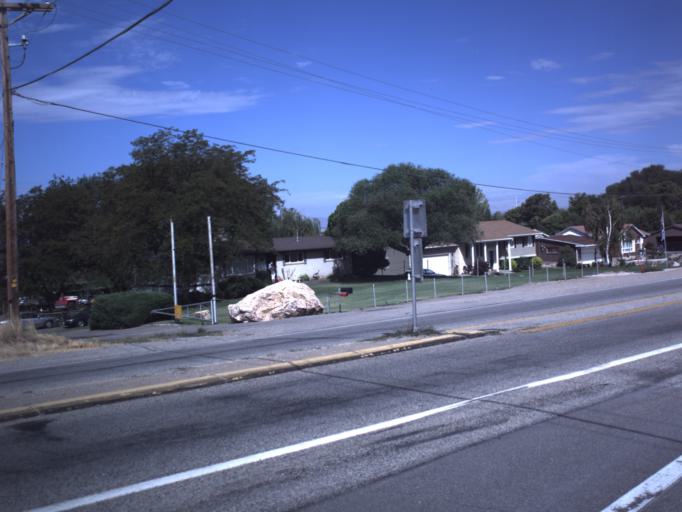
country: US
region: Utah
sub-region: Box Elder County
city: South Willard
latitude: 41.3462
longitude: -112.0332
